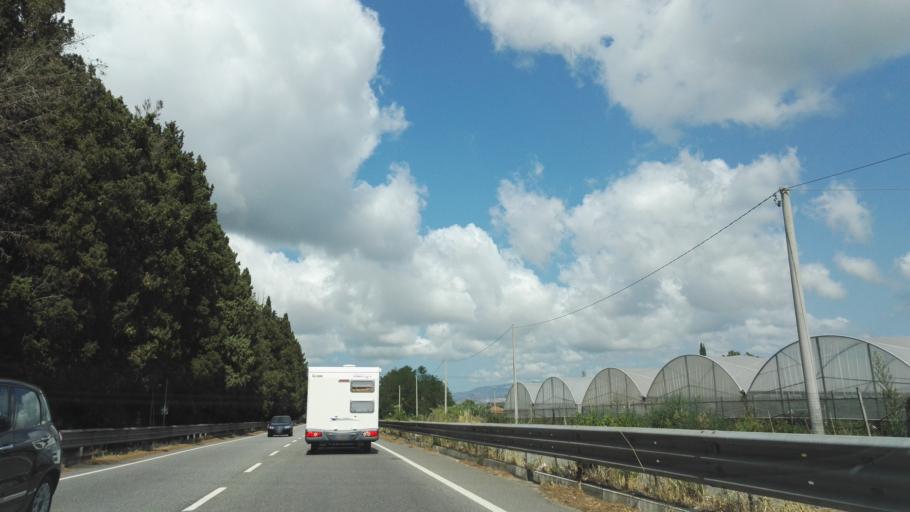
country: IT
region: Calabria
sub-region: Provincia di Reggio Calabria
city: Melicucco
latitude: 38.4598
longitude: 16.0188
